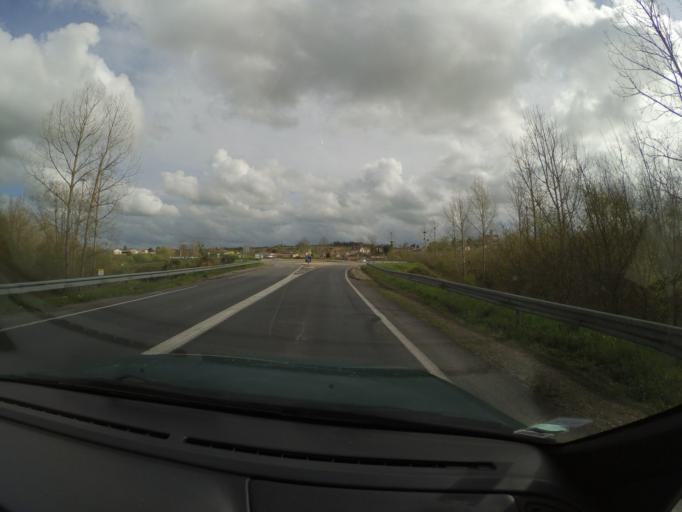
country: FR
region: Pays de la Loire
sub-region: Departement de Maine-et-Loire
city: Lire
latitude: 47.3480
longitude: -1.1648
